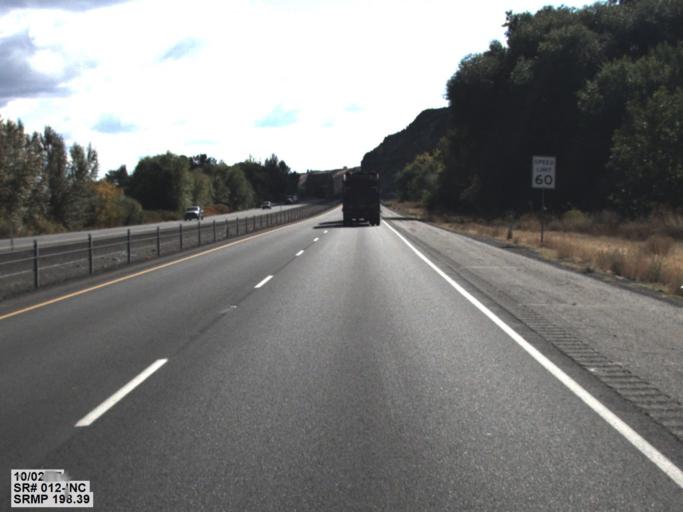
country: US
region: Washington
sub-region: Yakima County
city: Gleed
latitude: 46.6352
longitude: -120.5904
